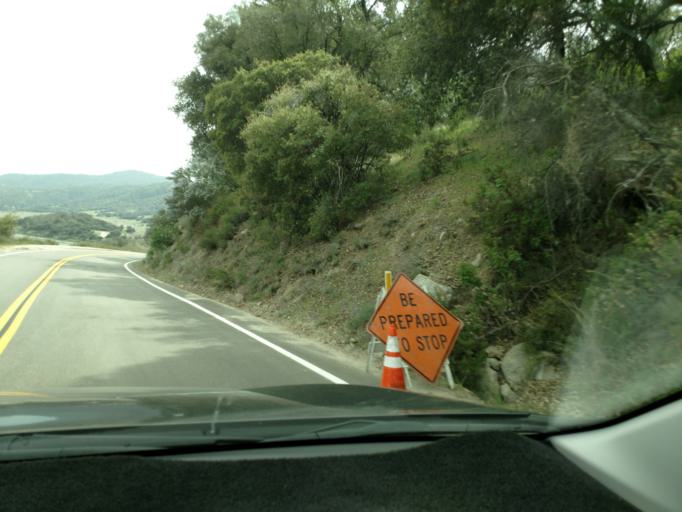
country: US
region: California
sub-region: Riverside County
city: Aguanga
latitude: 33.2469
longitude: -116.7645
